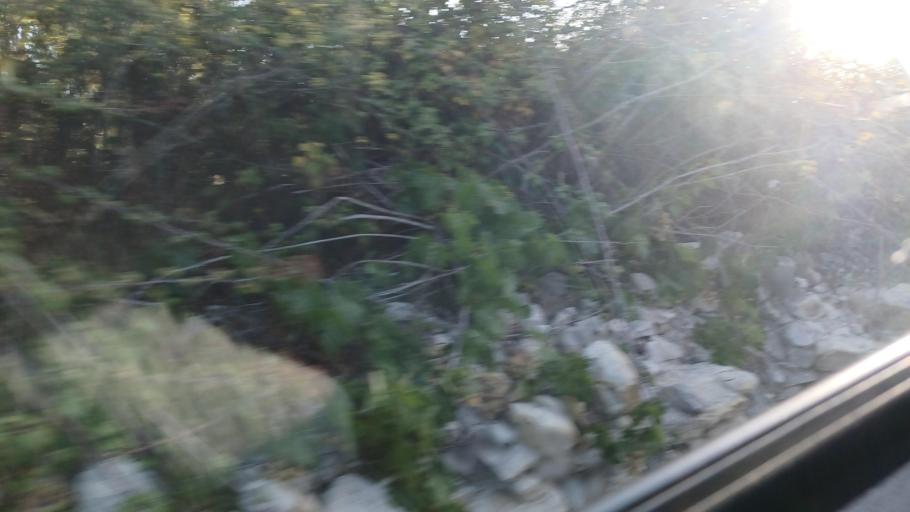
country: CY
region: Pafos
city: Mesogi
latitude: 34.8341
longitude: 32.4836
